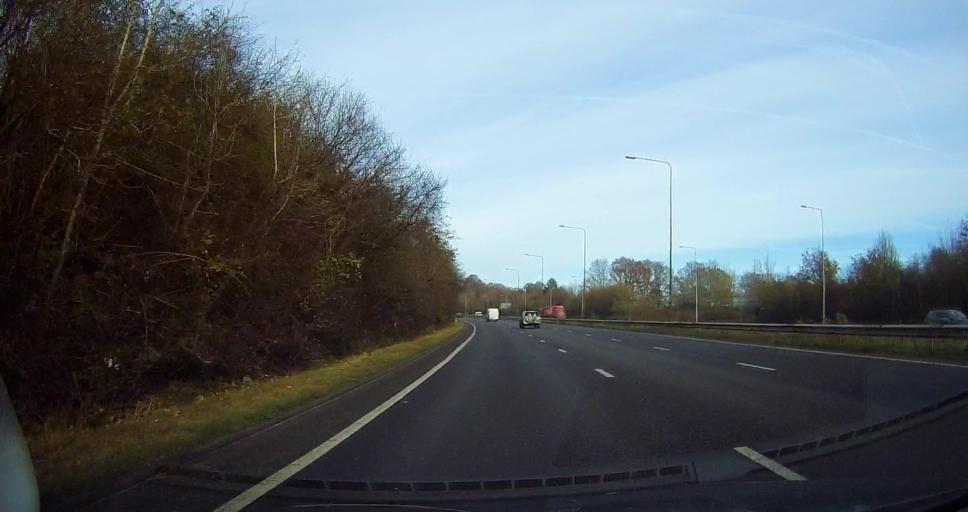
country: GB
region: England
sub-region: West Sussex
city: Cuckfield
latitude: 50.9969
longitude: -0.1964
